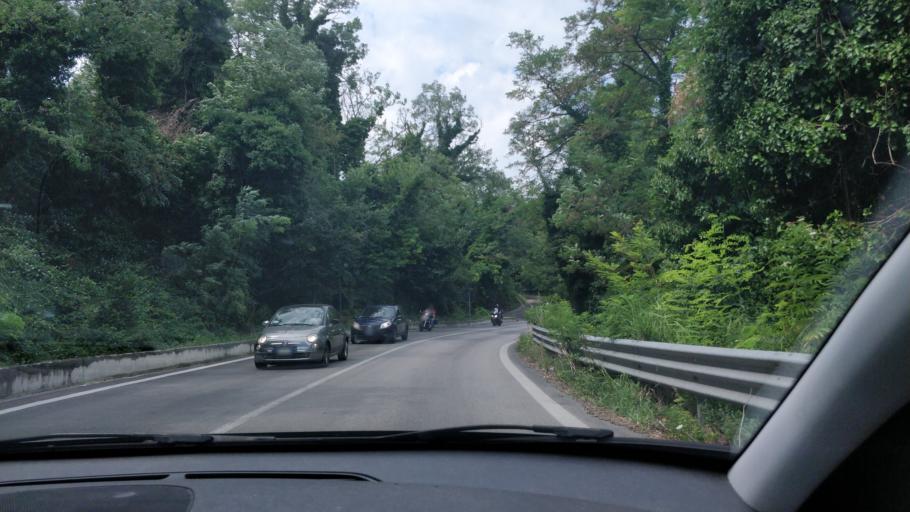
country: IT
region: Abruzzo
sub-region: Provincia di Chieti
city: Marina di San Vito
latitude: 42.3238
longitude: 14.4180
